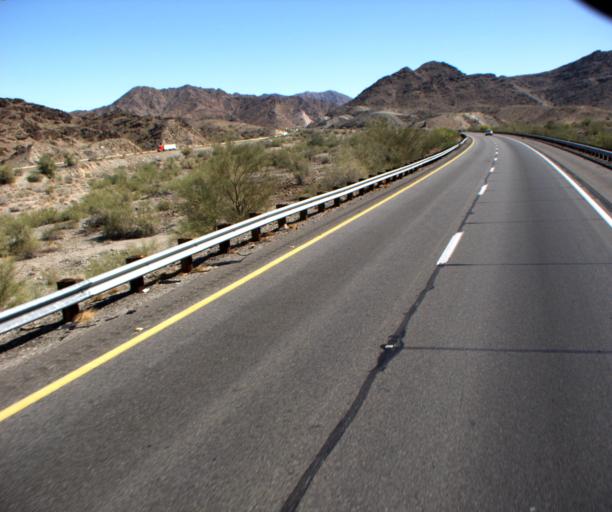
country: US
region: Arizona
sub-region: La Paz County
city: Ehrenberg
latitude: 33.6342
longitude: -114.3933
